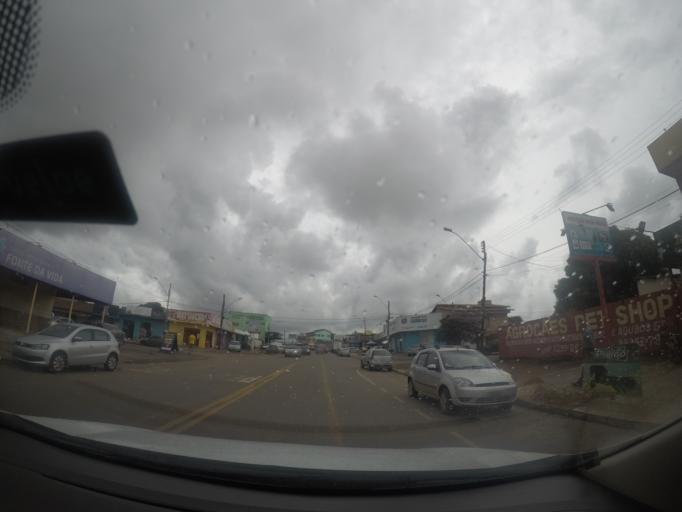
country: BR
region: Goias
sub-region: Trindade
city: Trindade
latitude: -16.6436
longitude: -49.3909
